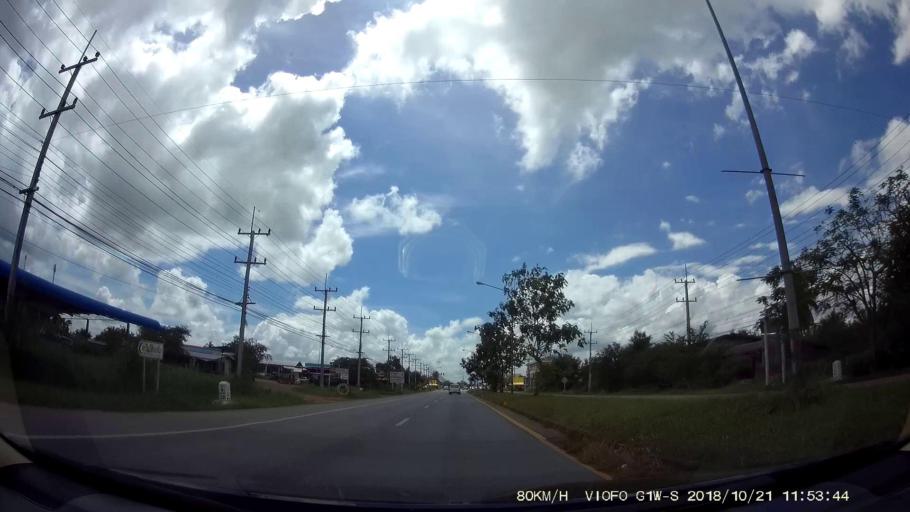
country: TH
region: Chaiyaphum
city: Chatturat
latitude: 15.5922
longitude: 101.9045
